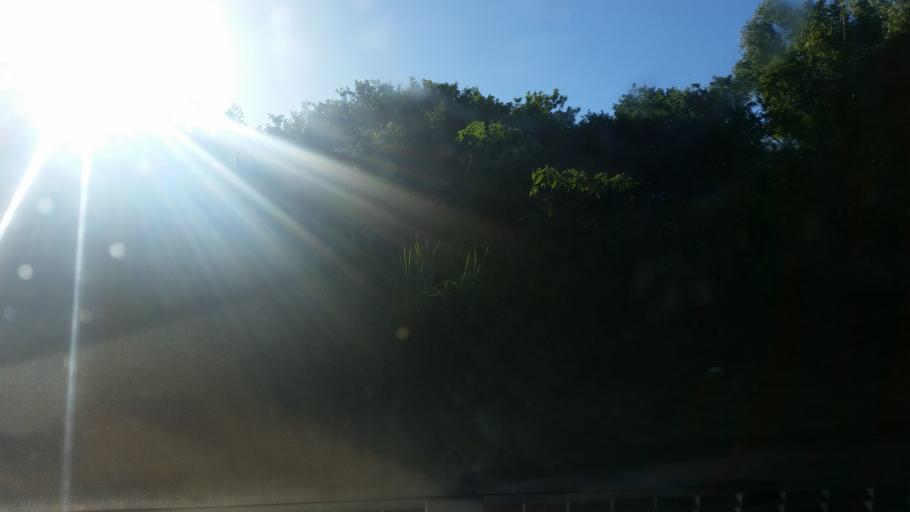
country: RE
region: Reunion
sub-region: Reunion
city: Sainte-Marie
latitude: -20.9367
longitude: 55.5313
